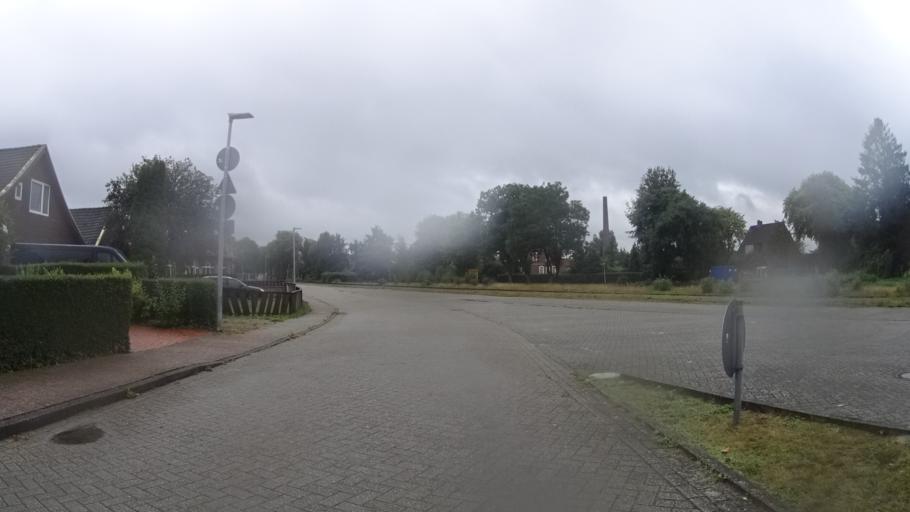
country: DE
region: Lower Saxony
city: Bunde
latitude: 53.1813
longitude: 7.2704
